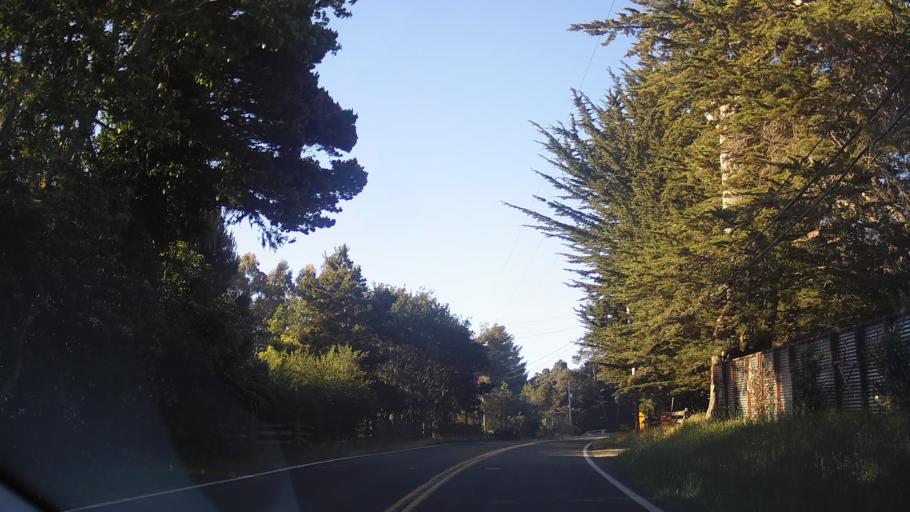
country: US
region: California
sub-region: Mendocino County
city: Fort Bragg
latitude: 39.4973
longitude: -123.7803
